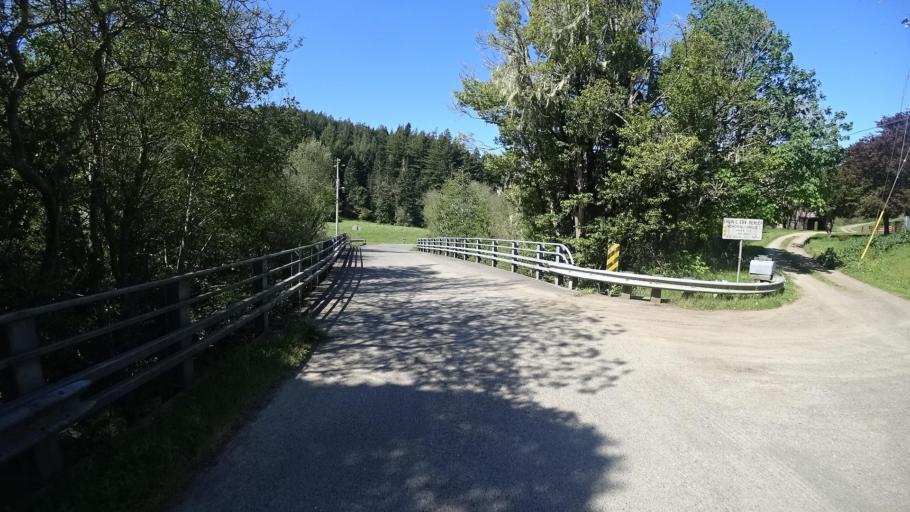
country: US
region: California
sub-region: Humboldt County
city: Fortuna
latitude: 40.5290
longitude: -124.1785
